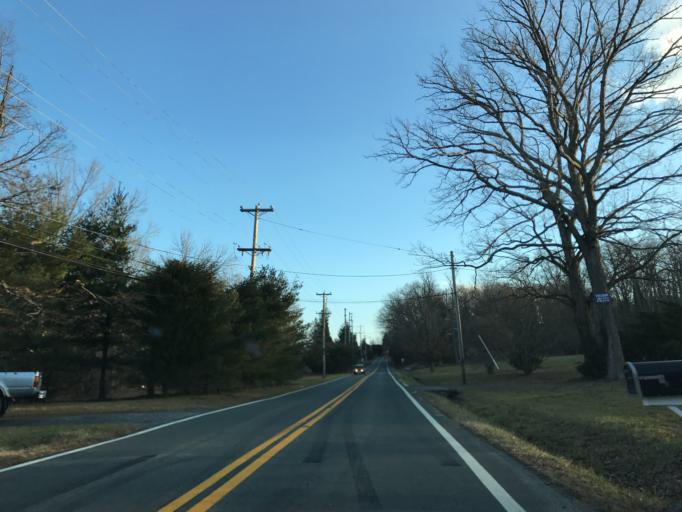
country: US
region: Maryland
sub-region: Cecil County
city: Charlestown
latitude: 39.5173
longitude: -75.9534
